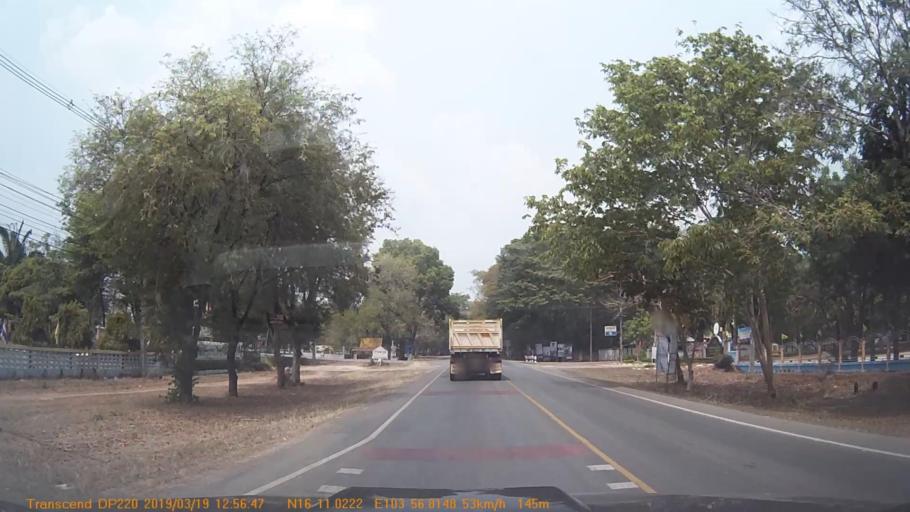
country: TH
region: Roi Et
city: Waeng
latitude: 16.1839
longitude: 103.9469
